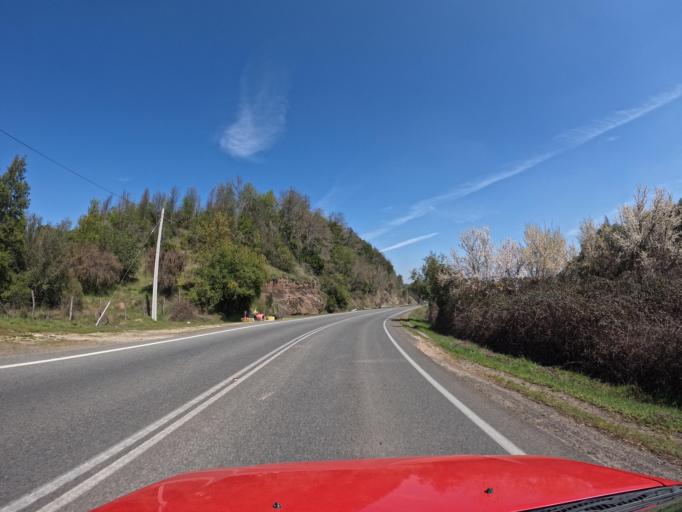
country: CL
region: Maule
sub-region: Provincia de Talca
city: San Clemente
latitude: -35.4662
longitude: -71.2712
